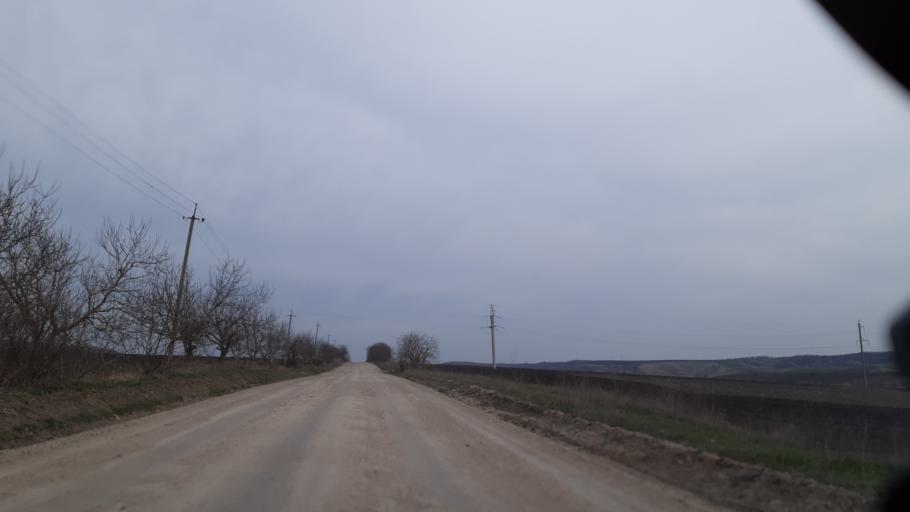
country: MD
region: Soldanesti
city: Soldanesti
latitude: 47.7028
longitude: 28.7188
